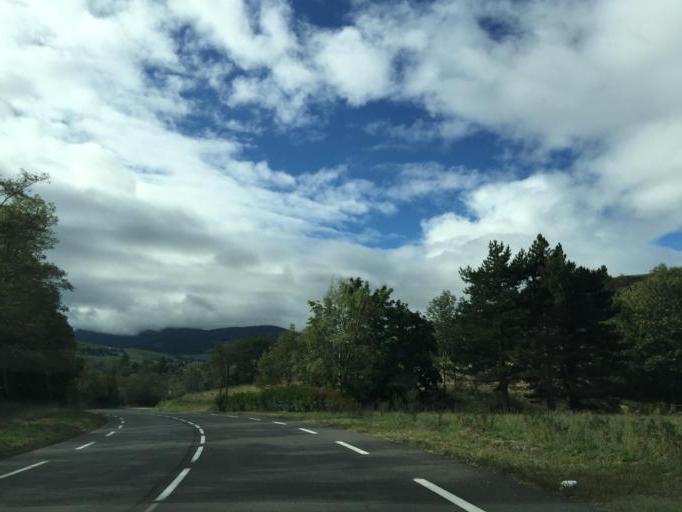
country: FR
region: Rhone-Alpes
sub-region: Departement de la Loire
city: Saint-Paul-en-Jarez
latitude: 45.4567
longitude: 4.5815
